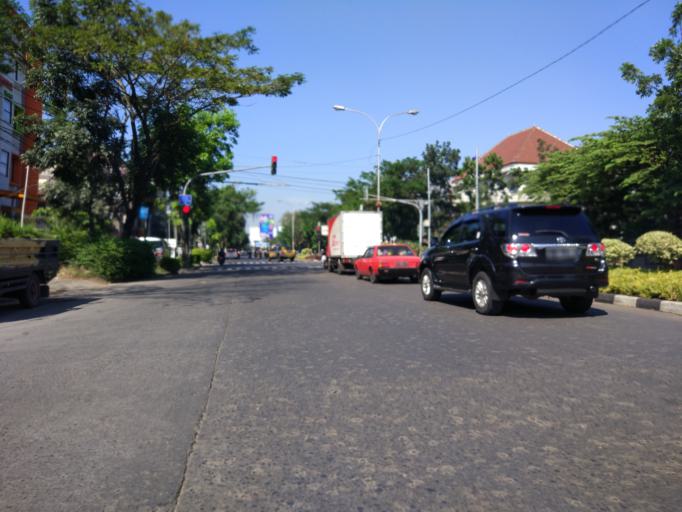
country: ID
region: West Java
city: Bandung
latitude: -6.9292
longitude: 107.6266
